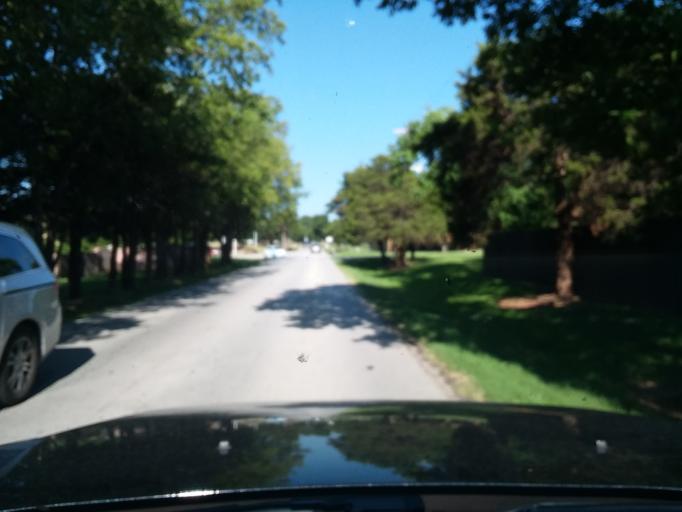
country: US
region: Texas
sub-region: Denton County
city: Double Oak
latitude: 33.0626
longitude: -97.0929
